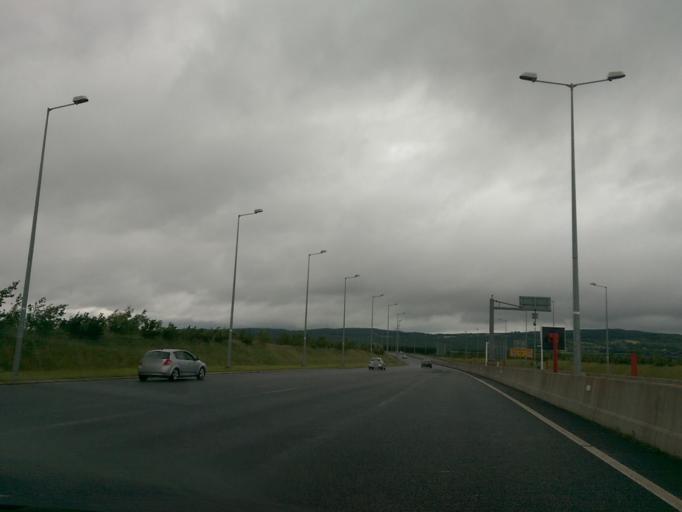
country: IE
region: Munster
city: Moyross
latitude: 52.6710
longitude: -8.7010
